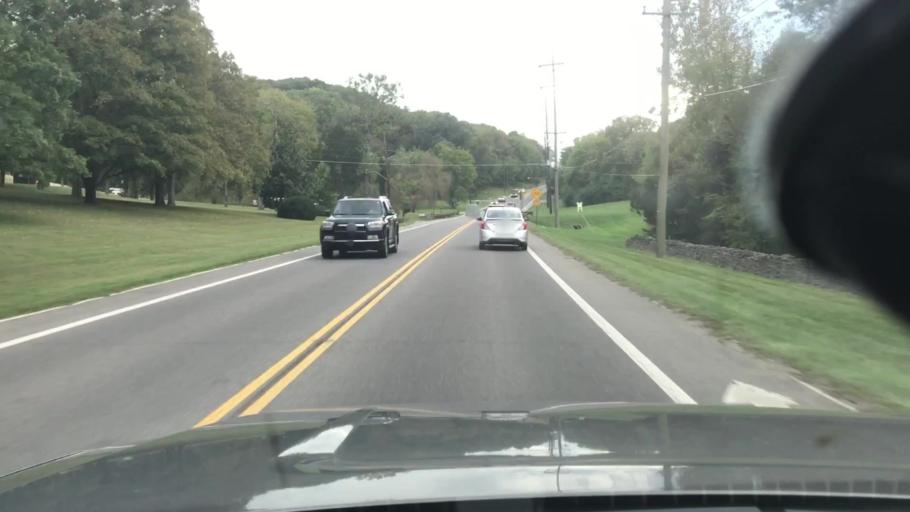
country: US
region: Tennessee
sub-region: Davidson County
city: Forest Hills
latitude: 36.0699
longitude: -86.8424
